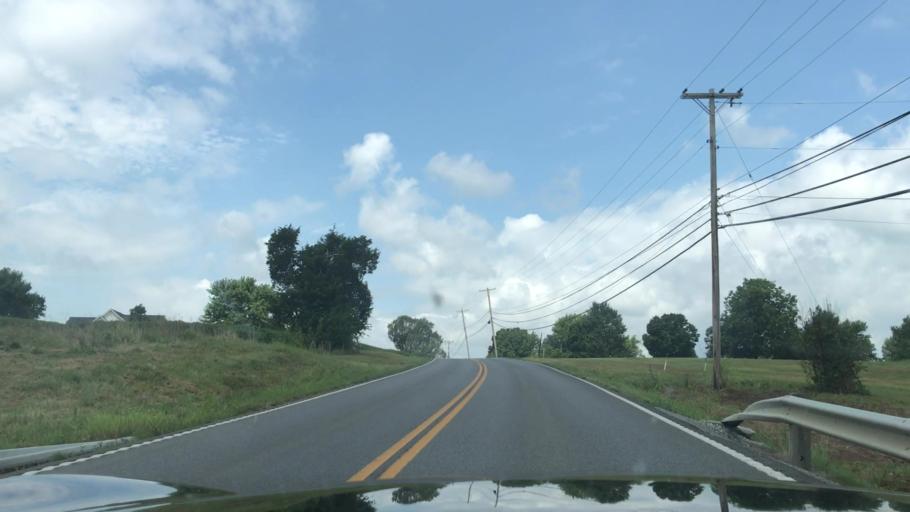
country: US
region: Kentucky
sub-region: Muhlenberg County
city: Greenville
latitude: 37.2046
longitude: -87.1452
